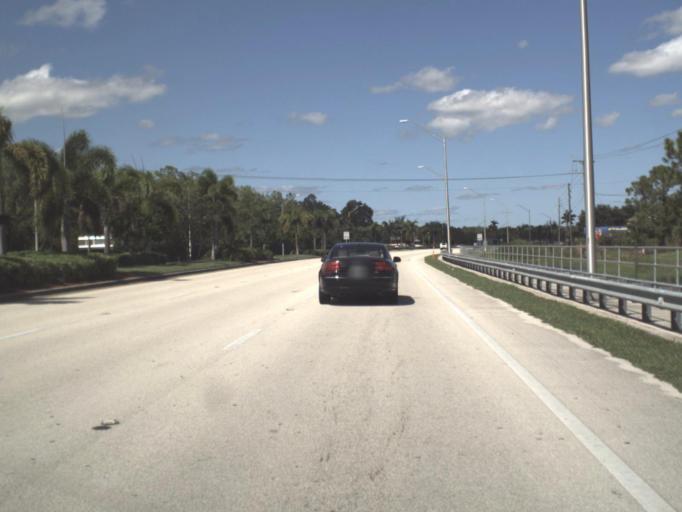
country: US
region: Florida
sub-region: Collier County
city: Naples Manor
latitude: 26.0758
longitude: -81.7186
